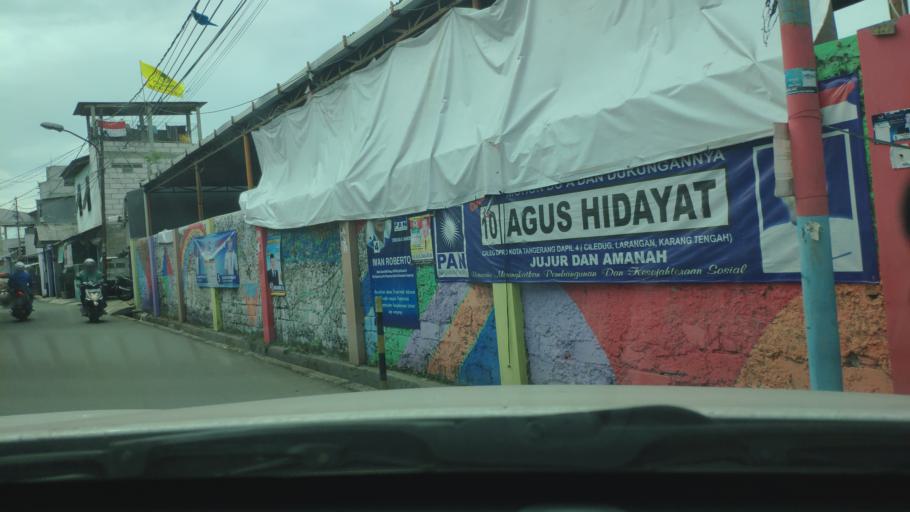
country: ID
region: West Java
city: Ciputat
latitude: -6.2222
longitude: 106.7056
